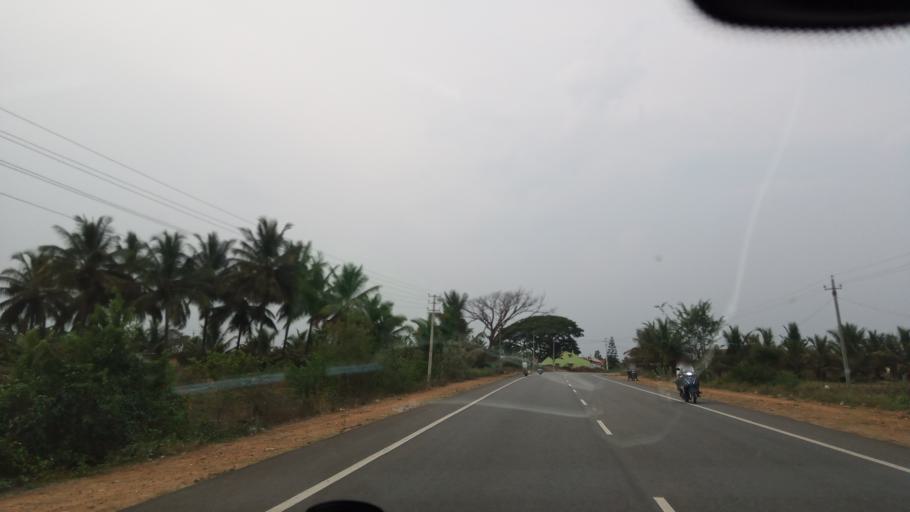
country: IN
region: Karnataka
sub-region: Mandya
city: Nagamangala
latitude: 12.7316
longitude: 76.7179
